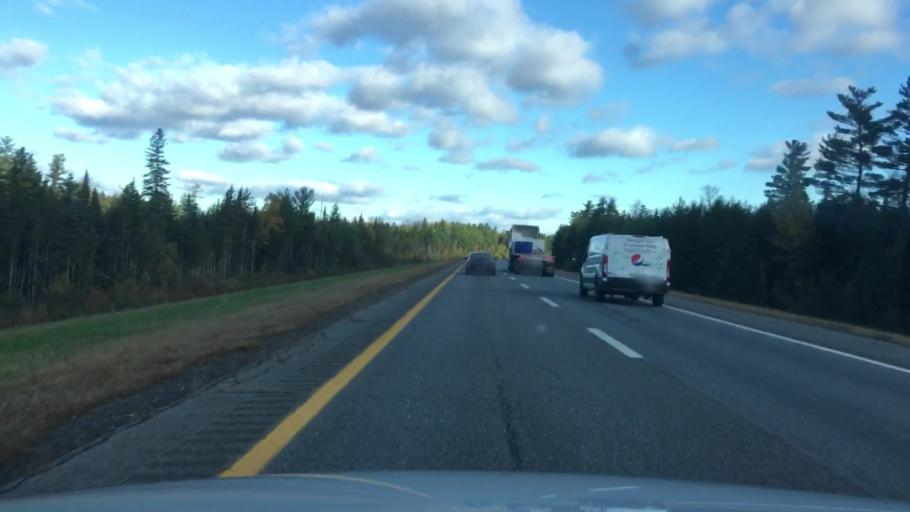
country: US
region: Maine
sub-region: Penobscot County
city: Greenbush
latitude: 45.1468
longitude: -68.7026
